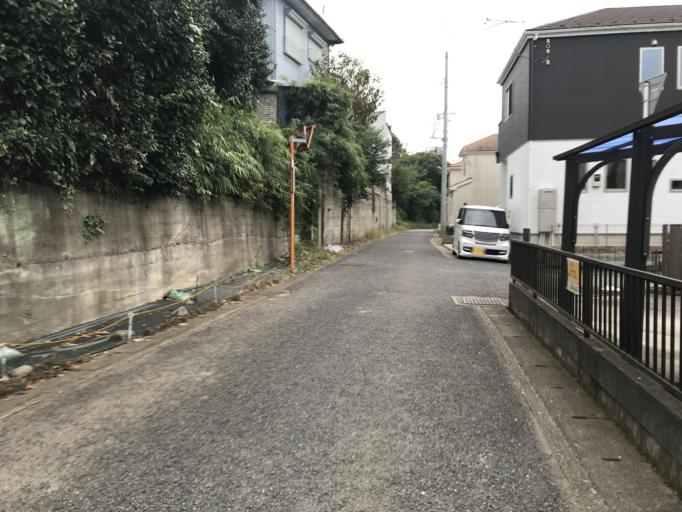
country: JP
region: Saitama
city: Shiraoka
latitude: 36.0078
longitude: 139.6565
